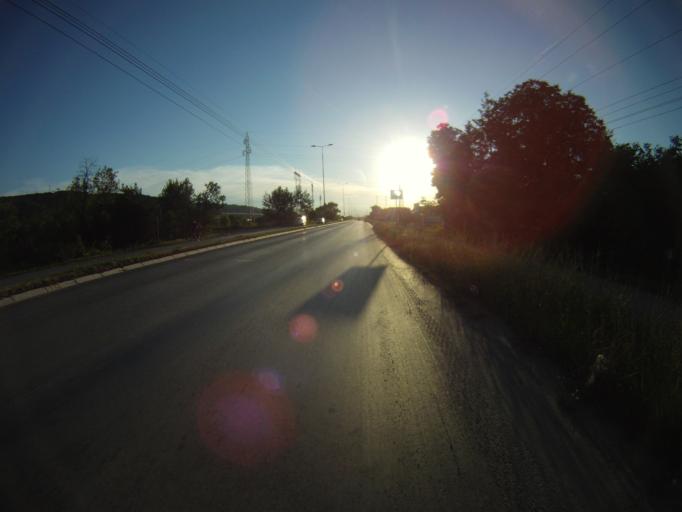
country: RS
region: Central Serbia
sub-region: Nisavski Okrug
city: Niska Banja
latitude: 43.3037
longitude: 21.9759
